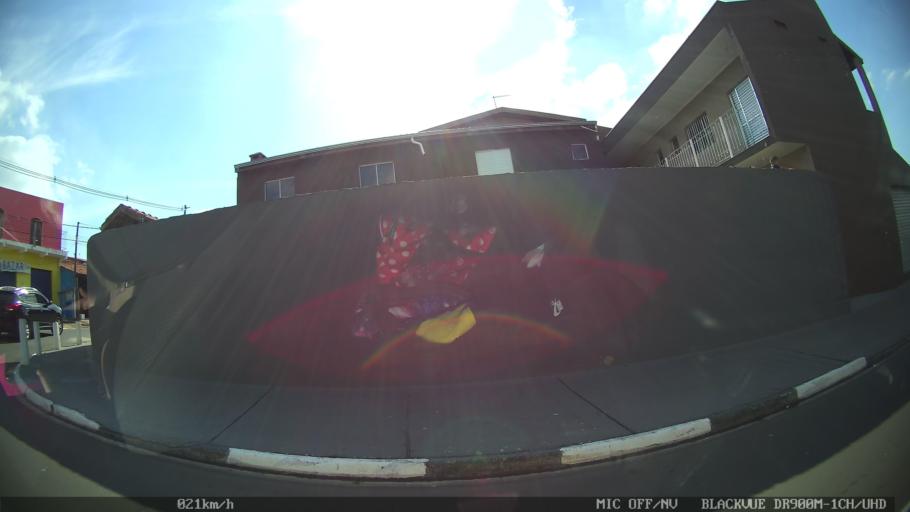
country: BR
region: Sao Paulo
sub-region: Hortolandia
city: Hortolandia
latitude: -22.8986
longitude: -47.2441
